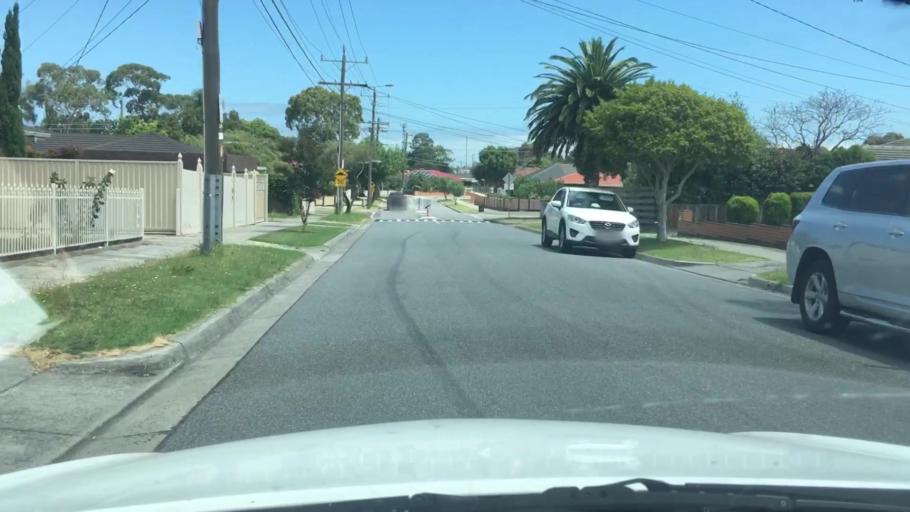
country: AU
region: Victoria
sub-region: Greater Dandenong
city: Keysborough
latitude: -37.9932
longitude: 145.1786
